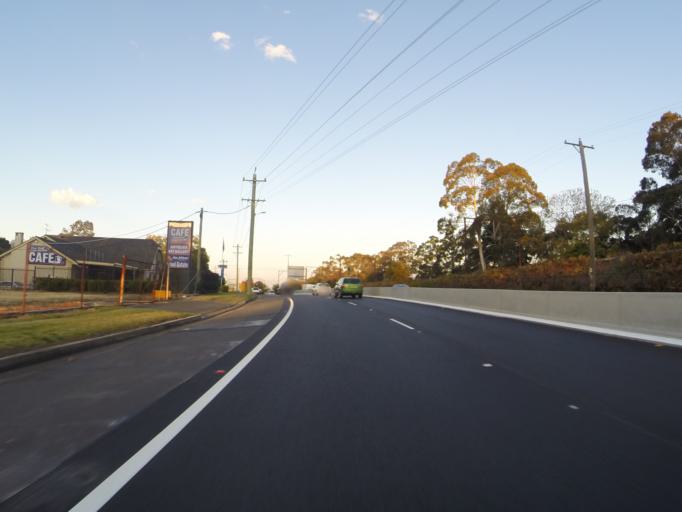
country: AU
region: New South Wales
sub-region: Blue Mountains Municipality
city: Blaxland
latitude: -33.7024
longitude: 150.5766
